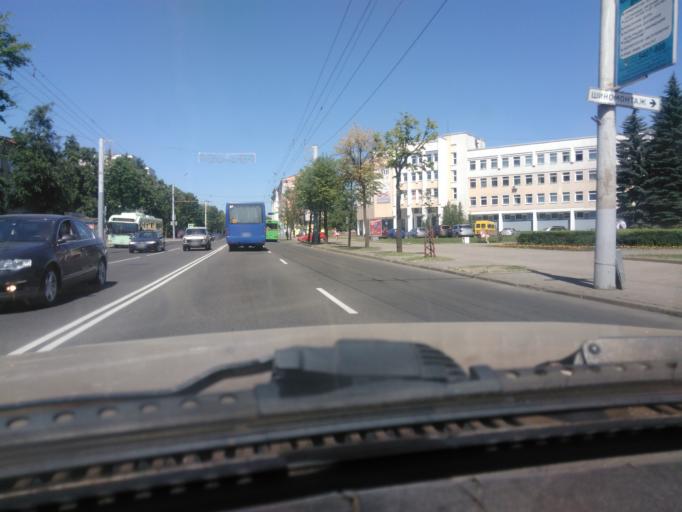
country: BY
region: Mogilev
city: Mahilyow
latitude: 53.9160
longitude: 30.3421
